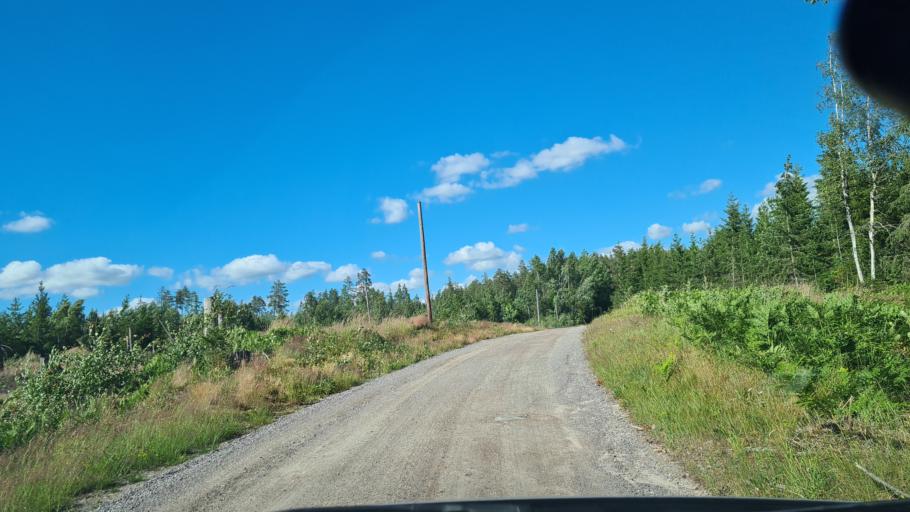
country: SE
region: OEstergoetland
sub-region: Norrkopings Kommun
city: Krokek
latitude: 58.6986
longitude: 16.4270
